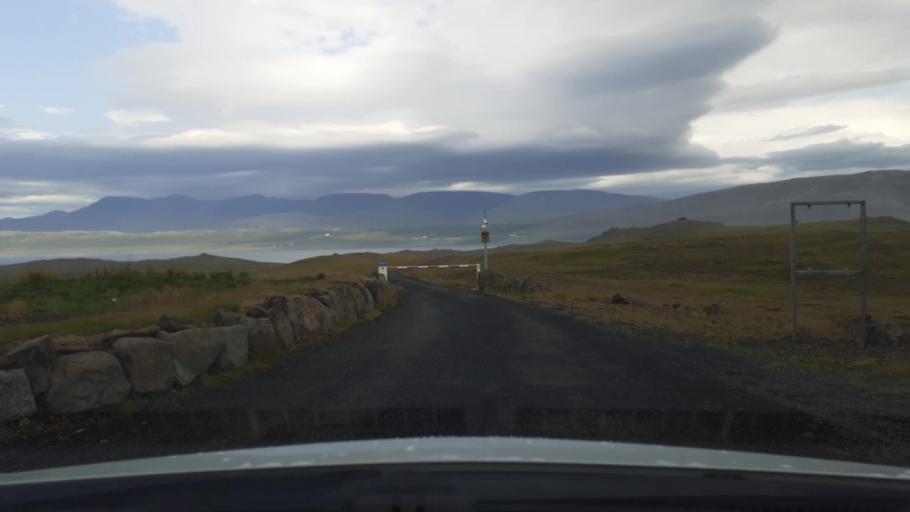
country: IS
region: Capital Region
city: Mosfellsbaer
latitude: 64.3645
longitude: -21.5755
